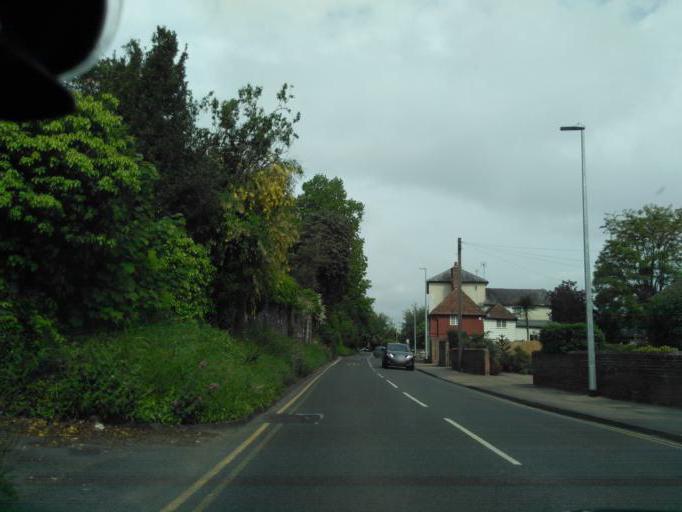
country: GB
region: England
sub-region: Kent
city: Canterbury
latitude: 51.2695
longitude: 1.0912
